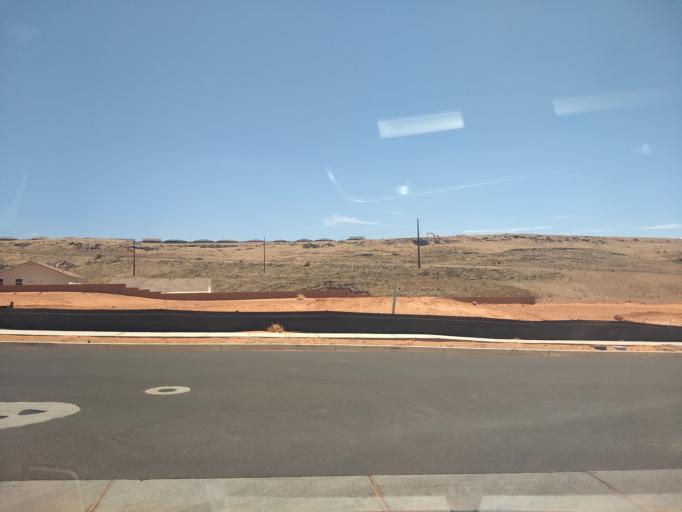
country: US
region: Utah
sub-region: Washington County
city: Washington
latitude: 37.1383
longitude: -113.4785
